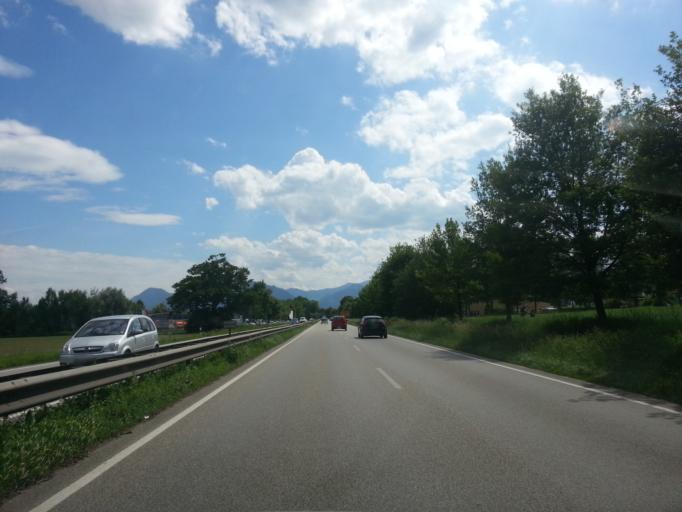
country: DE
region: Bavaria
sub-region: Upper Bavaria
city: Raubling
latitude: 47.8168
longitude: 12.1198
